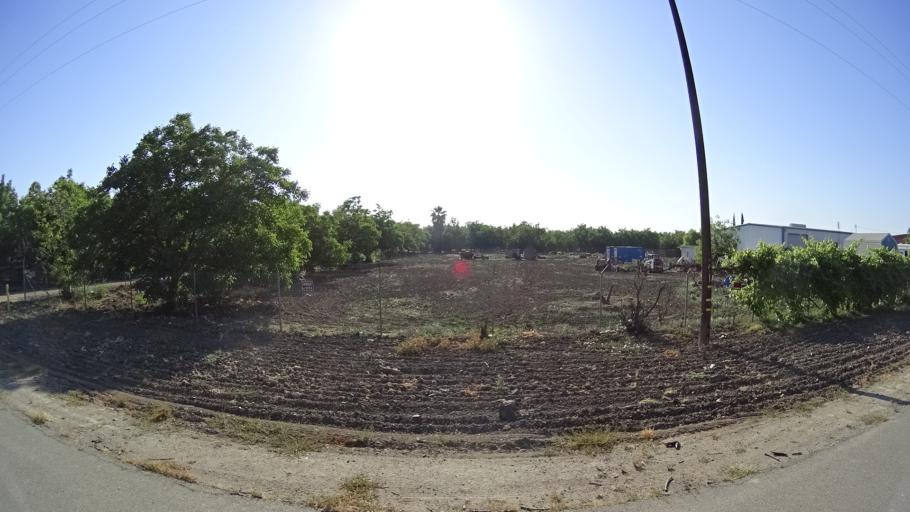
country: US
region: California
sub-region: Kings County
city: Armona
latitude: 36.3221
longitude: -119.7090
